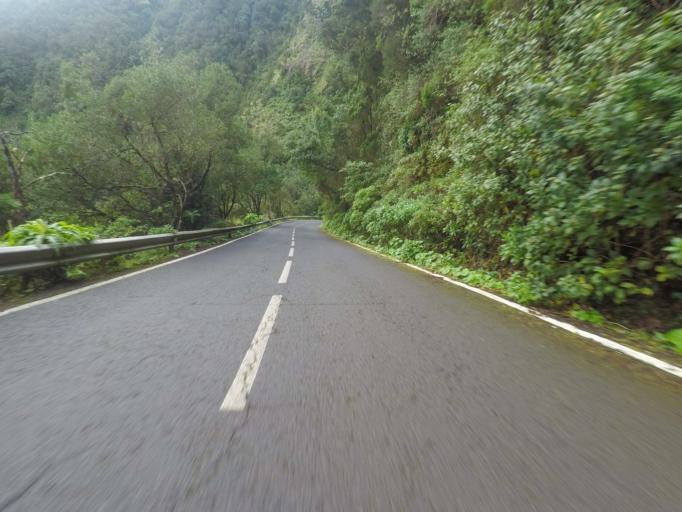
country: ES
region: Canary Islands
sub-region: Provincia de Santa Cruz de Tenerife
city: Hermigua
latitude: 28.1248
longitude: -17.2063
